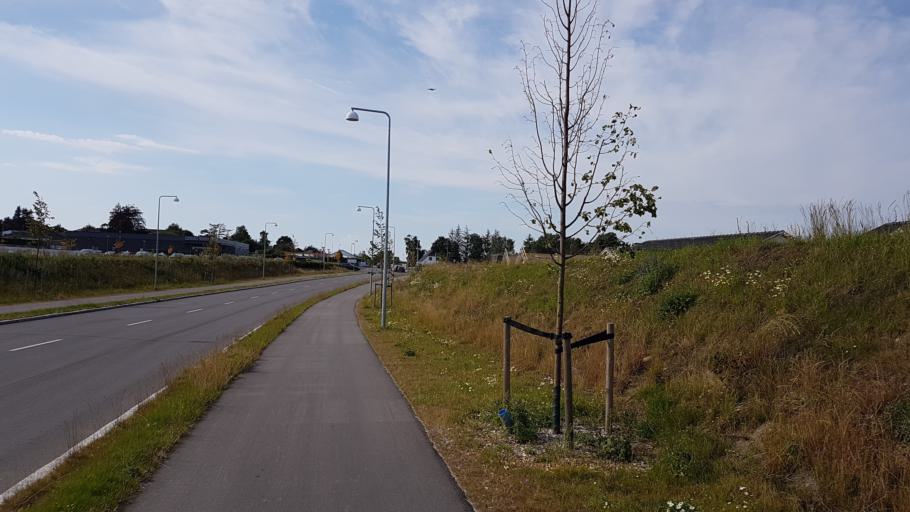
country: DK
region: Zealand
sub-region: Roskilde Kommune
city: Jyllinge
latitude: 55.7621
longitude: 12.1195
